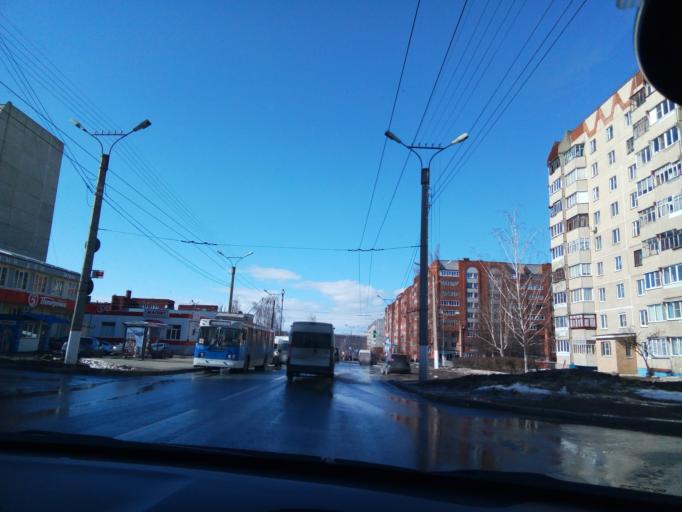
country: RU
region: Chuvashia
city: Novyye Lapsary
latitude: 56.1146
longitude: 47.1806
